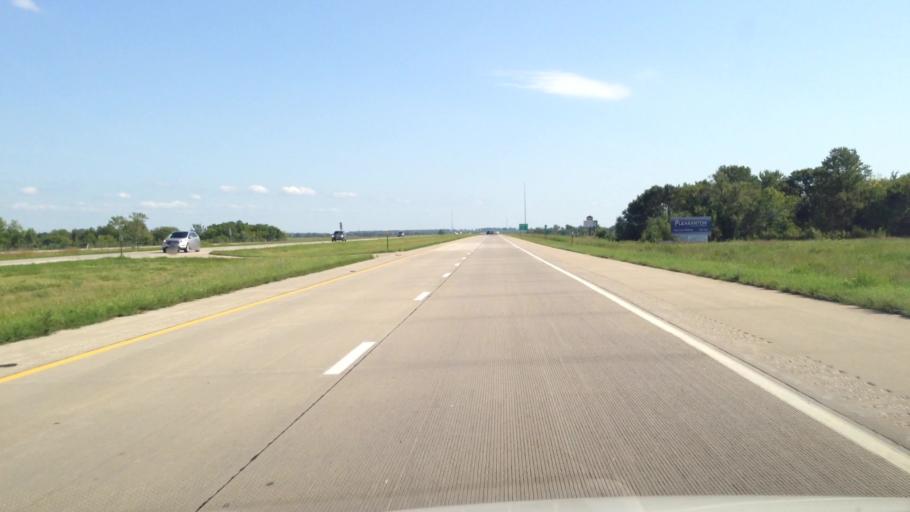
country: US
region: Kansas
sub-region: Linn County
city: Pleasanton
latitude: 38.1899
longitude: -94.7042
